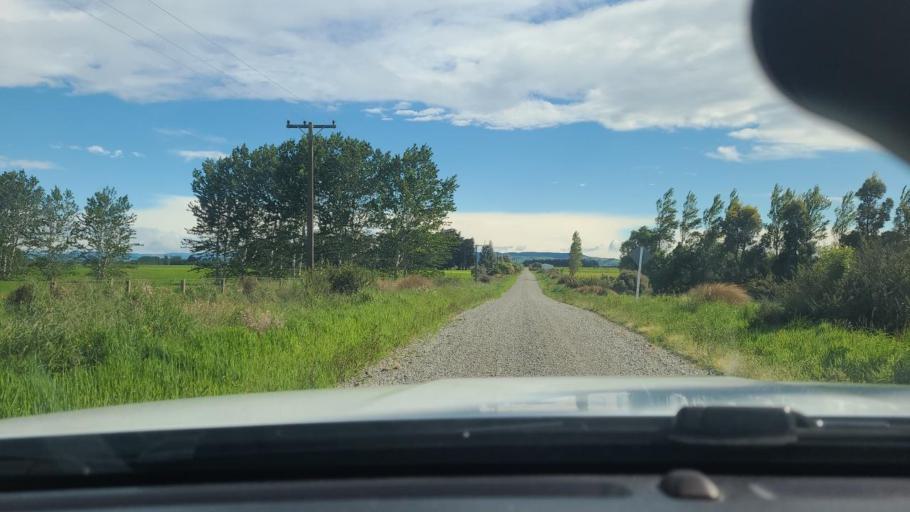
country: NZ
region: Southland
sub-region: Southland District
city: Winton
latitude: -46.1030
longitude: 168.2584
